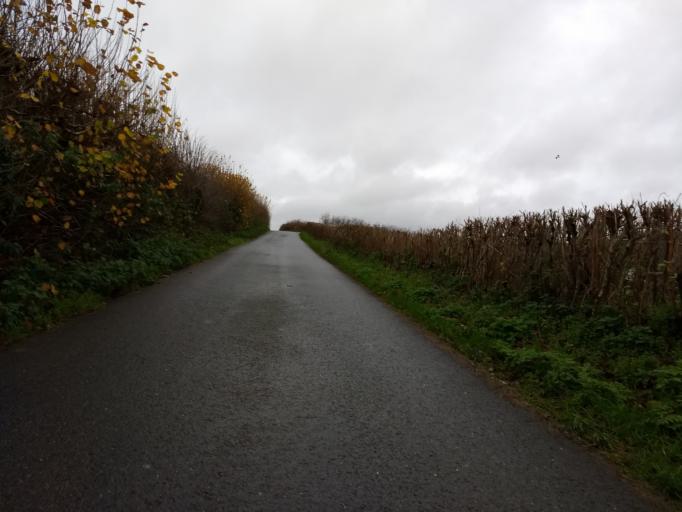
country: GB
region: England
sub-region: Isle of Wight
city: Newport
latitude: 50.6878
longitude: -1.2638
